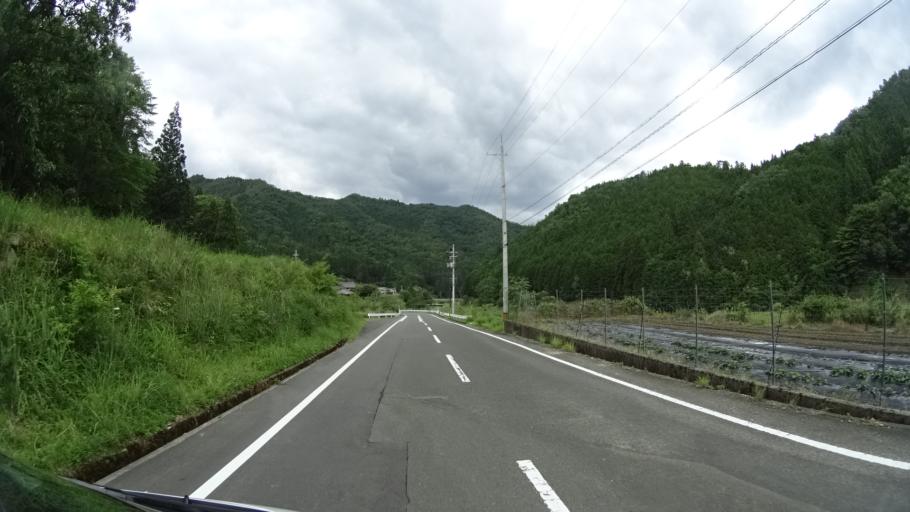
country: JP
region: Hyogo
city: Sasayama
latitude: 35.0549
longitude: 135.3983
